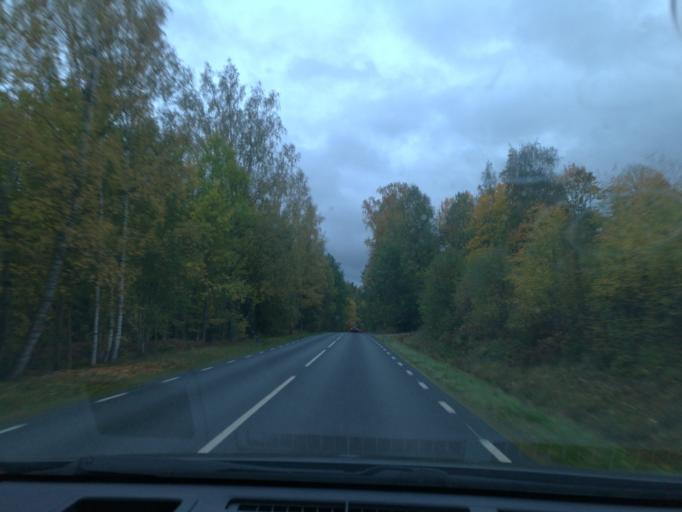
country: SE
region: Soedermanland
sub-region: Vingakers Kommun
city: Vingaker
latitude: 59.0703
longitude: 15.8914
